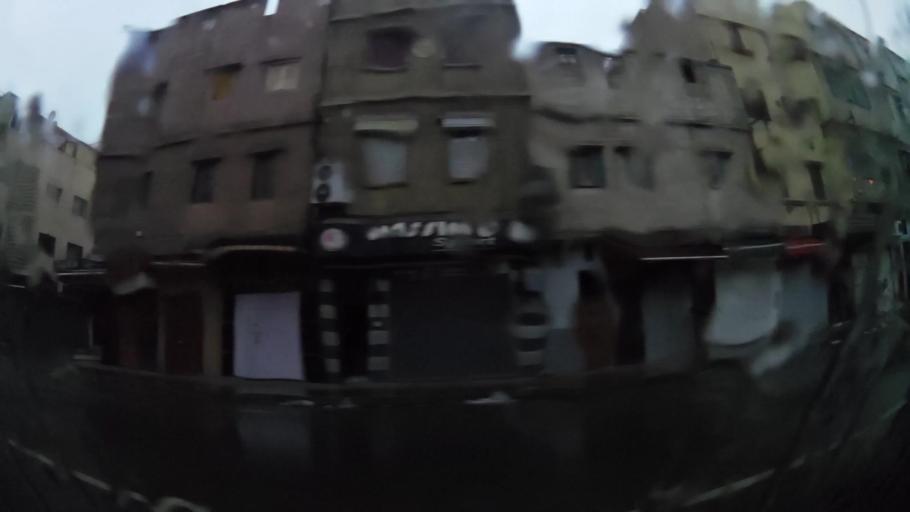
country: MA
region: Grand Casablanca
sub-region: Casablanca
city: Casablanca
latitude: 33.5647
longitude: -7.6004
